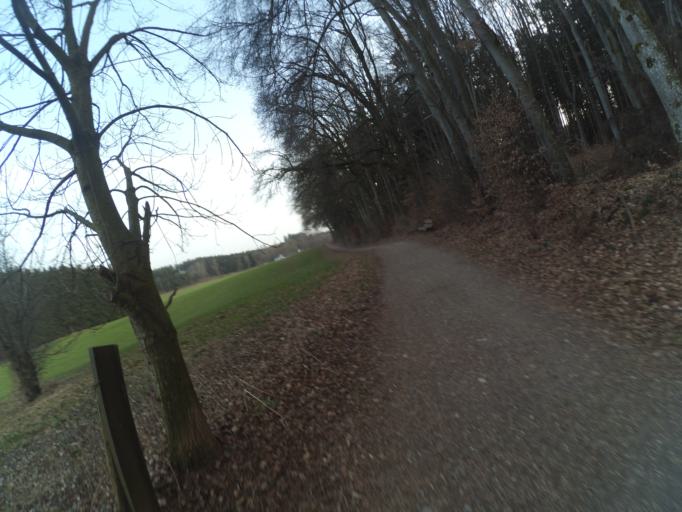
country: DE
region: Bavaria
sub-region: Swabia
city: Bad Worishofen
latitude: 47.9989
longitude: 10.5696
